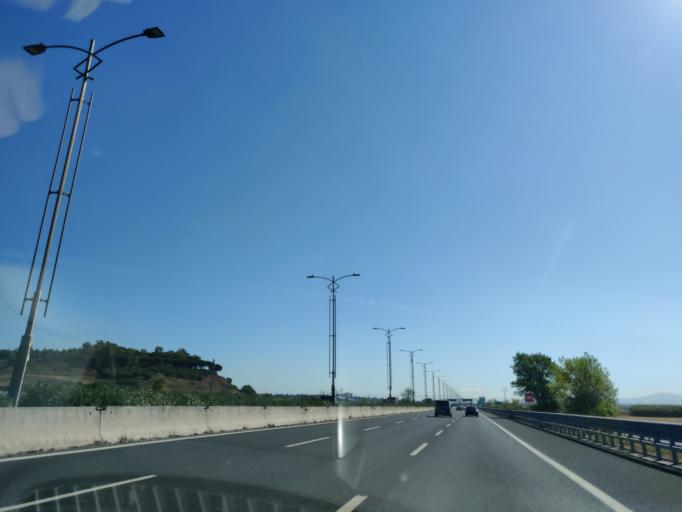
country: IT
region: Latium
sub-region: Citta metropolitana di Roma Capitale
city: Ponte Galeria-La Pisana
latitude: 41.8150
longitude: 12.3549
